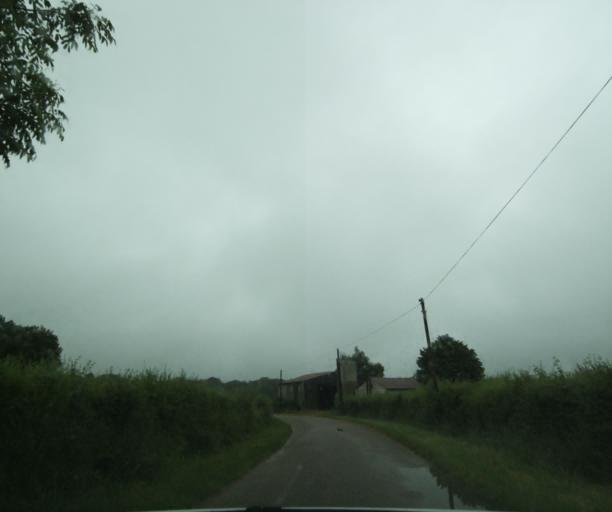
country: FR
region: Bourgogne
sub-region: Departement de Saone-et-Loire
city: Charolles
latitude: 46.4581
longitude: 4.2408
